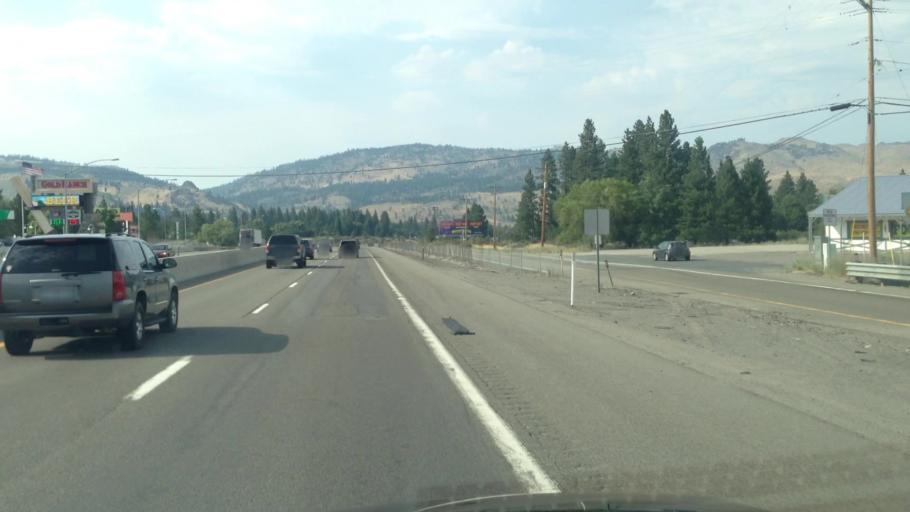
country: US
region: Nevada
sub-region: Washoe County
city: Verdi
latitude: 39.5011
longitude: -119.9983
